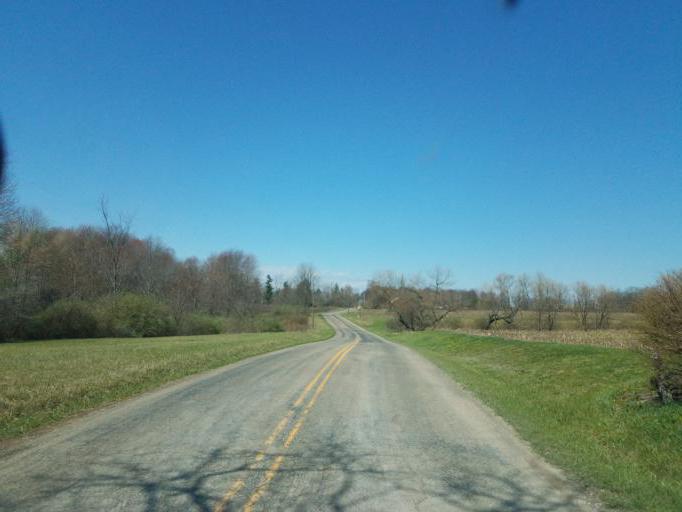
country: US
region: Ohio
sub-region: Knox County
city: Gambier
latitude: 40.3199
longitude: -82.3051
